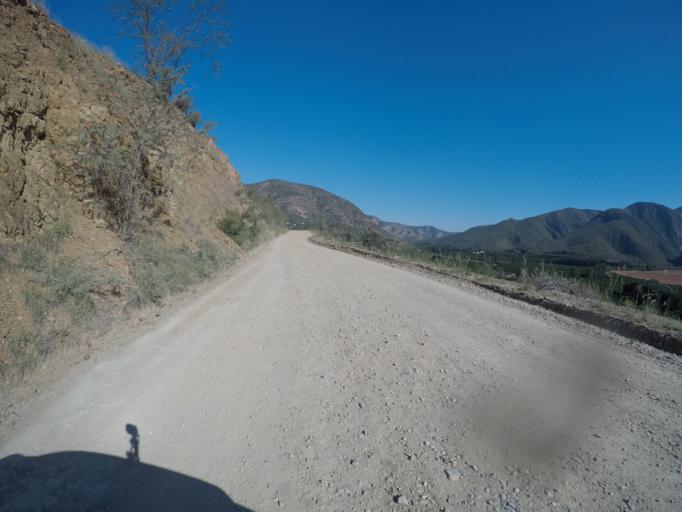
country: ZA
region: Eastern Cape
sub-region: Cacadu District Municipality
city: Kruisfontein
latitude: -33.6639
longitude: 24.5674
